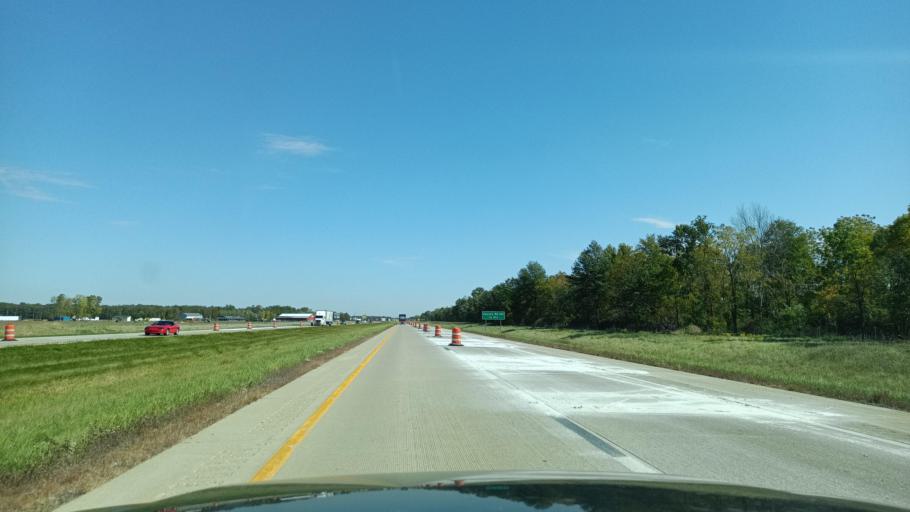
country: US
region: Ohio
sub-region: Defiance County
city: Defiance
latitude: 41.2486
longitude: -84.4866
